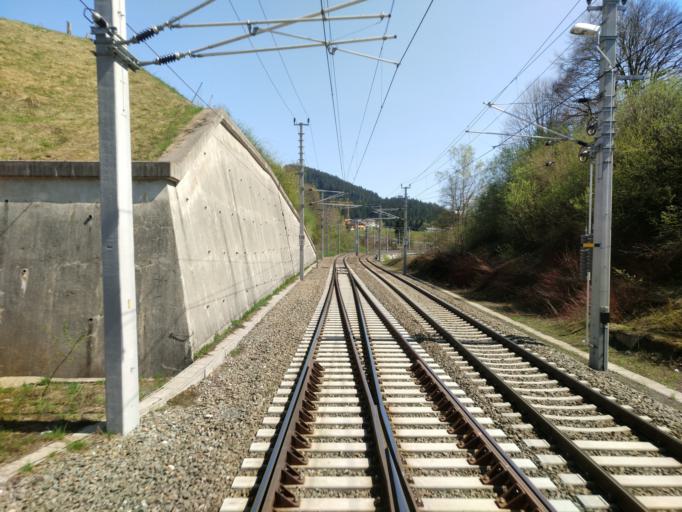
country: AT
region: Tyrol
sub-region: Politischer Bezirk Kitzbuhel
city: Fieberbrunn
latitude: 47.4899
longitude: 12.5329
